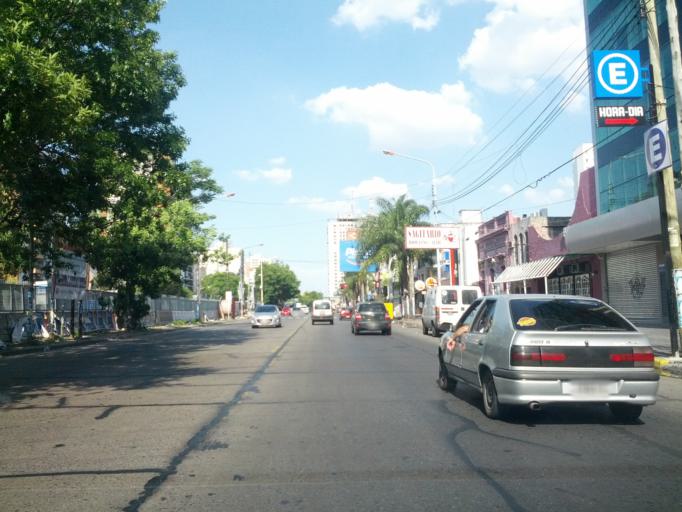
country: AR
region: Buenos Aires
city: San Justo
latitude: -34.6413
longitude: -58.5684
